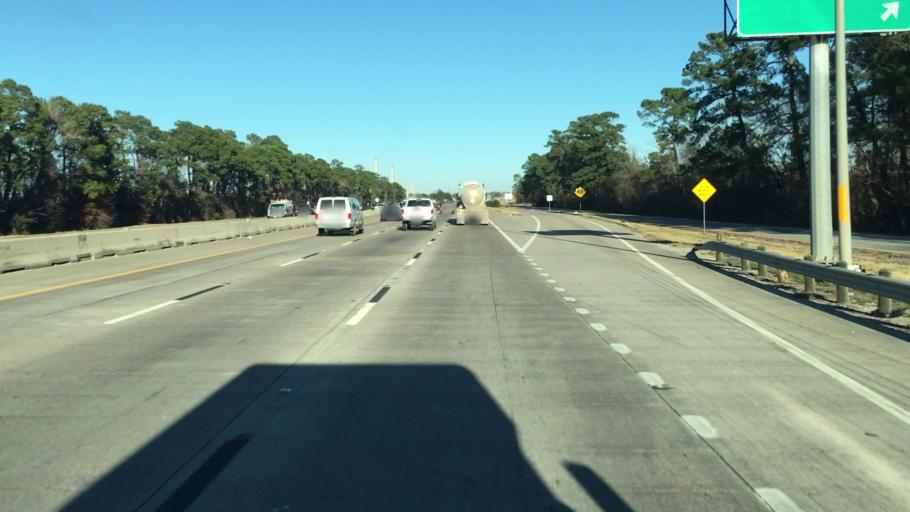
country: US
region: Texas
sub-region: Chambers County
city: Mont Belvieu
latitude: 29.8170
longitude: -94.9282
